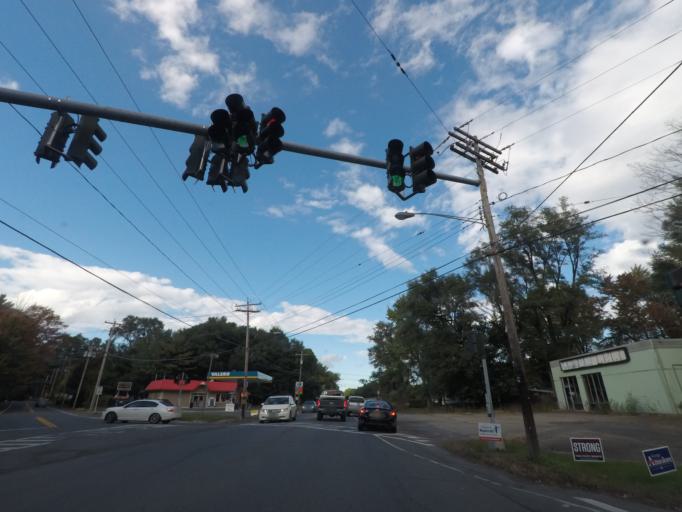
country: US
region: New York
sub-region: Schenectady County
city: Rotterdam
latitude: 42.7544
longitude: -73.9436
